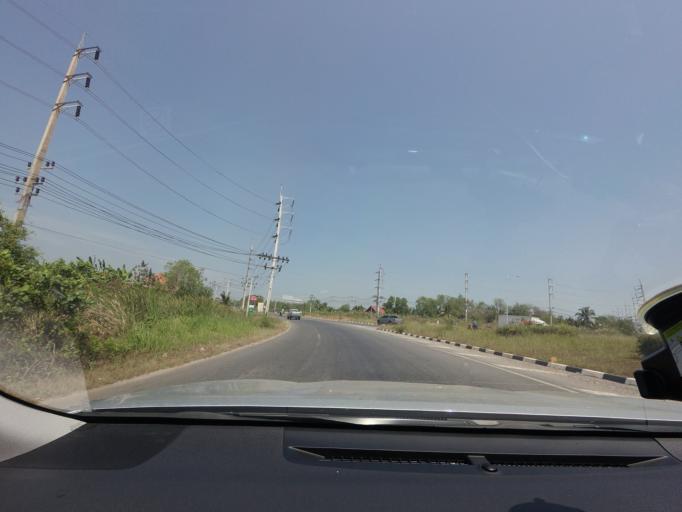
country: TH
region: Surat Thani
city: Surat Thani
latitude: 9.1640
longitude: 99.3714
